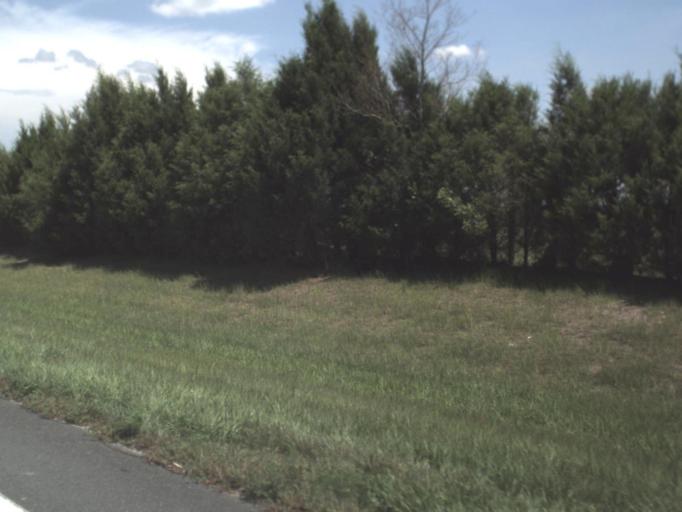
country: US
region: Florida
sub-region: Lafayette County
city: Mayo
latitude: 30.1289
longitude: -83.2842
